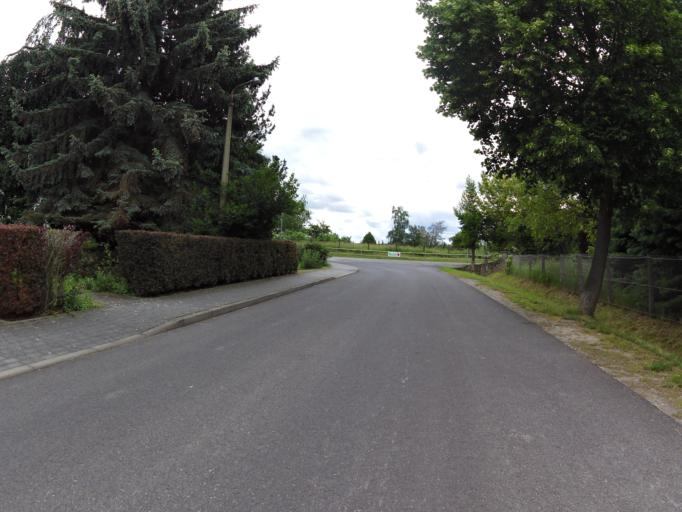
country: DE
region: Thuringia
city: Oberdorla
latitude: 51.1607
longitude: 10.4206
